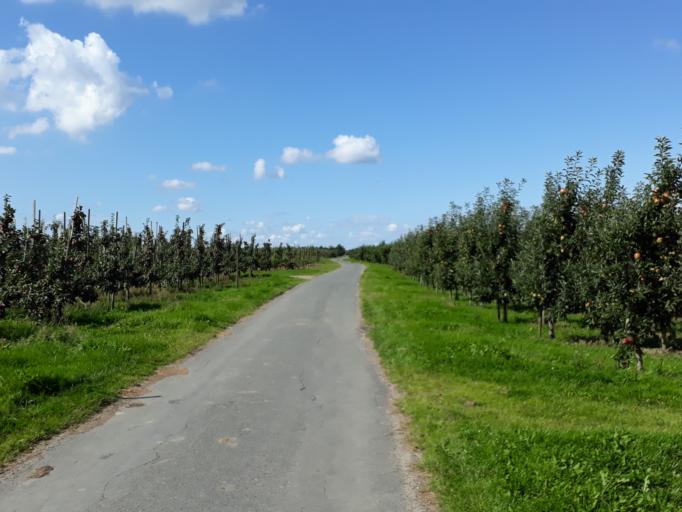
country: DE
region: Lower Saxony
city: Mittelnkirchen
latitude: 53.5440
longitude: 9.6335
